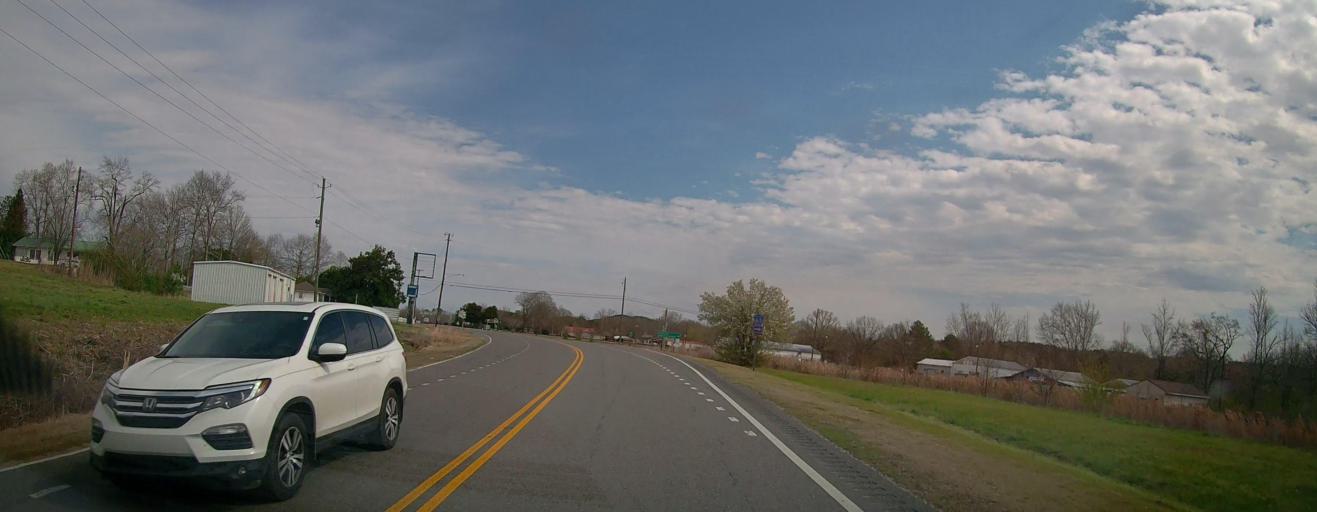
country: US
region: Alabama
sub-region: Walker County
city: Carbon Hill
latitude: 33.8905
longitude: -87.5337
